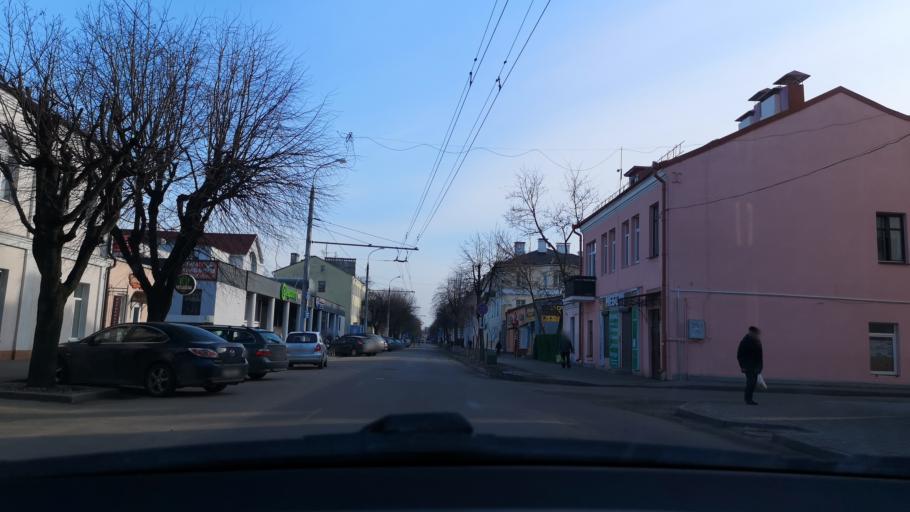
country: BY
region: Brest
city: Brest
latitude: 52.0984
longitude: 23.6848
